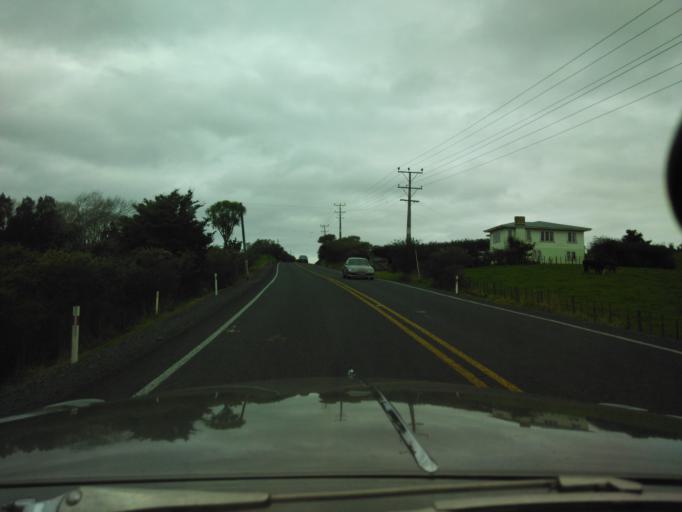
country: NZ
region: Auckland
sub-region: Auckland
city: Parakai
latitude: -36.6352
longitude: 174.5347
